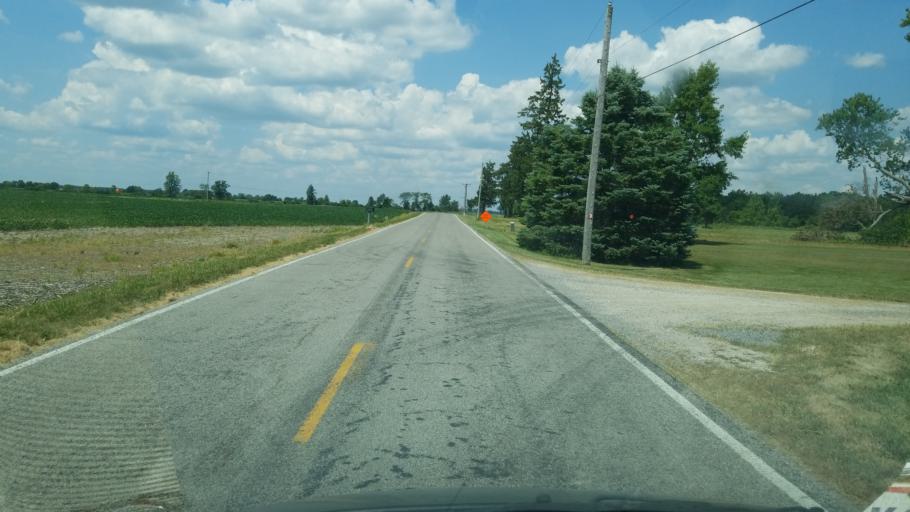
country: US
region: Ohio
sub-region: Champaign County
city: Mechanicsburg
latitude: 40.1162
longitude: -83.4696
